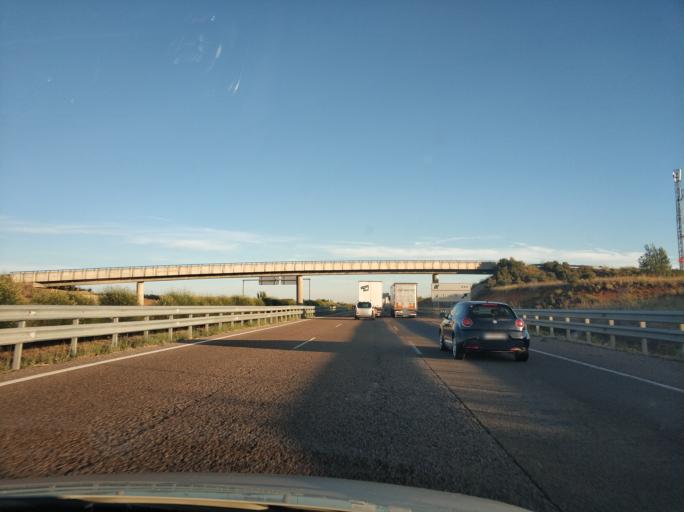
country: ES
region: Castille and Leon
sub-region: Provincia de Zamora
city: San Cristobal de Entrevinas
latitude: 42.0418
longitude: -5.6732
